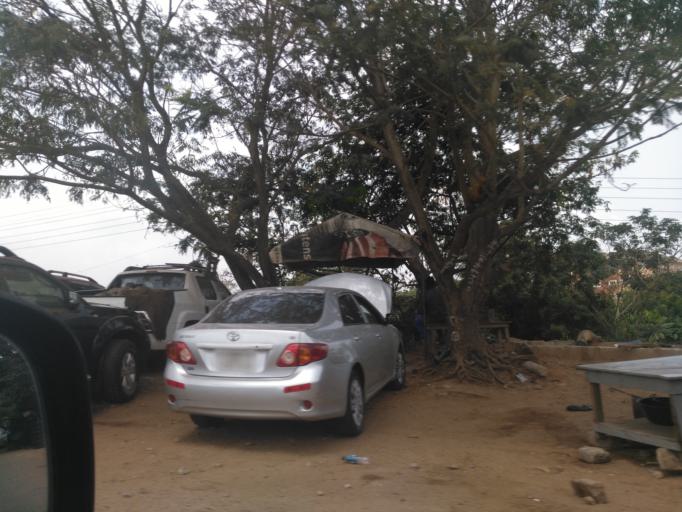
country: GH
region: Greater Accra
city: Accra
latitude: 5.5982
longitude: -0.1812
